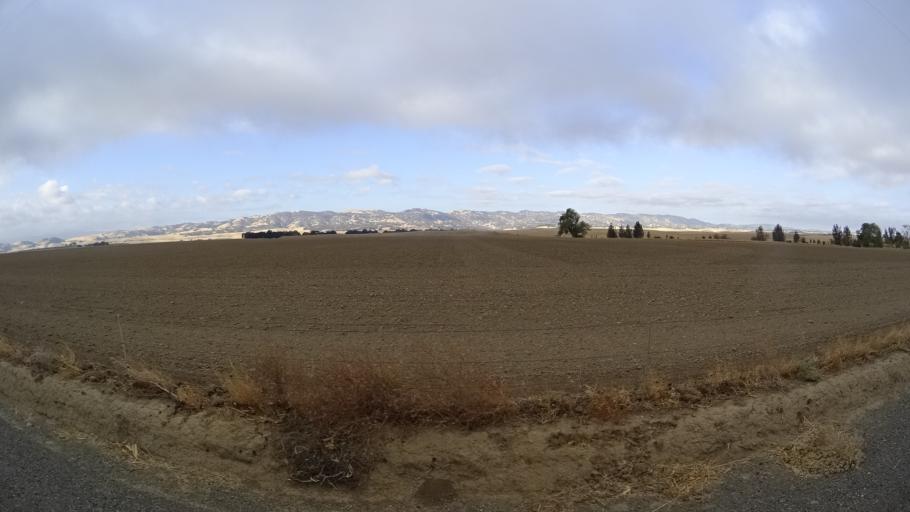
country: US
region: California
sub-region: Yolo County
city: Esparto
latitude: 38.7997
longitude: -122.0436
